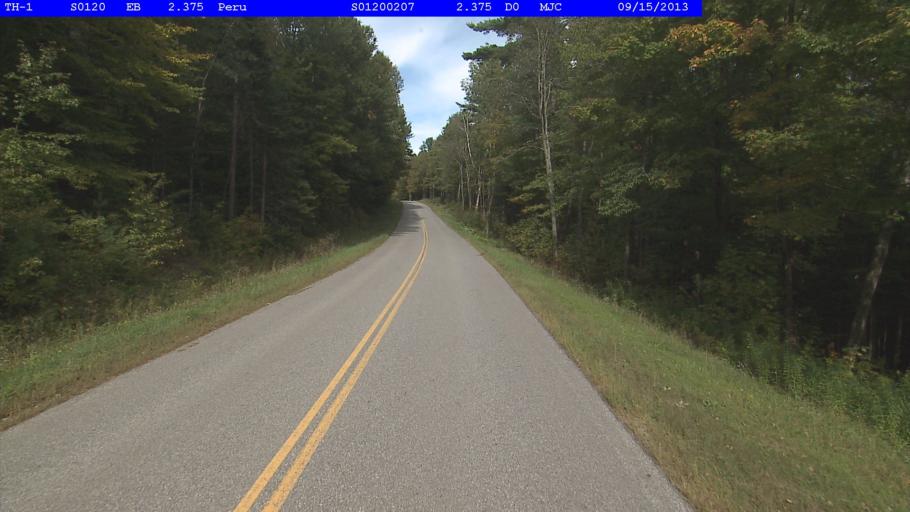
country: US
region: Vermont
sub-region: Bennington County
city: Manchester Center
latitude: 43.2556
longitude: -72.8829
